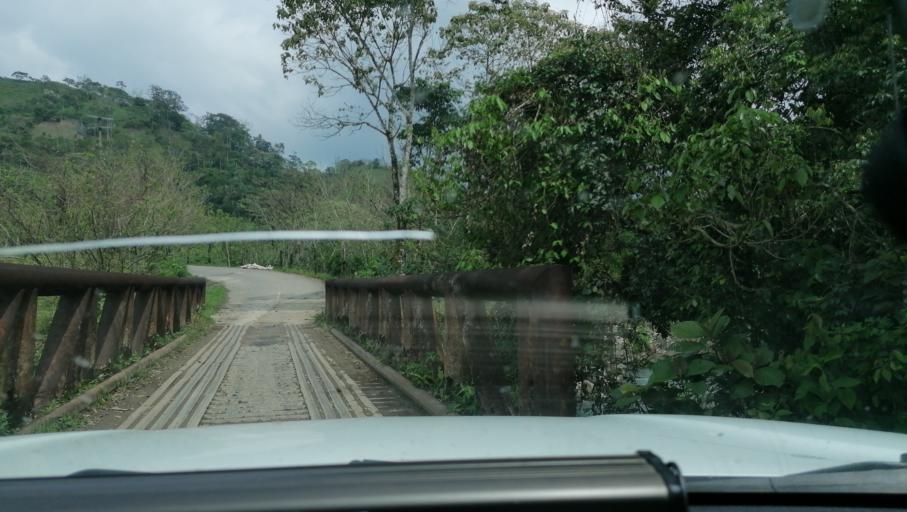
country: MX
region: Chiapas
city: Ocotepec
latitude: 17.3228
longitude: -93.1666
